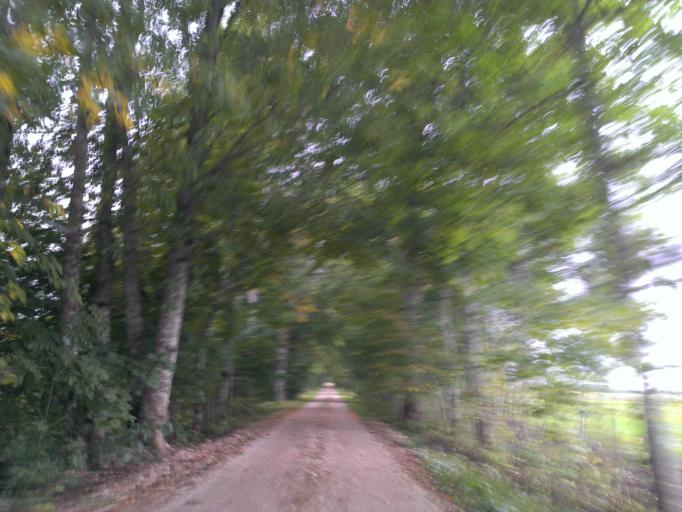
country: LV
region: Malpils
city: Malpils
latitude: 56.9050
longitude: 25.1255
